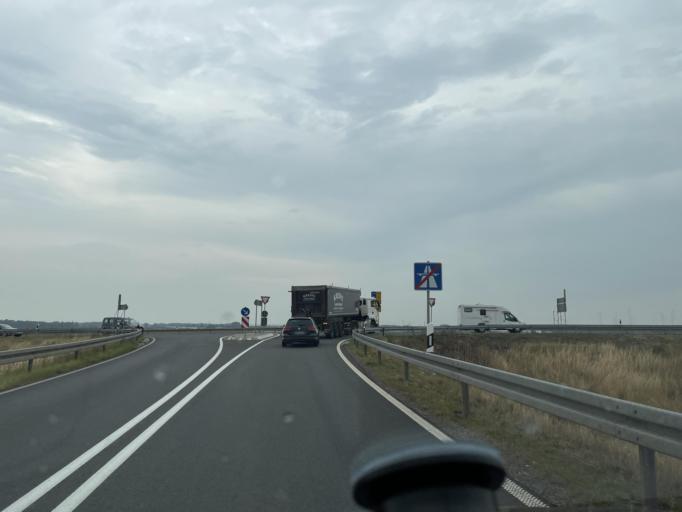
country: DE
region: Saxony-Anhalt
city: Giersleben
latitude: 51.7883
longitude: 11.5688
